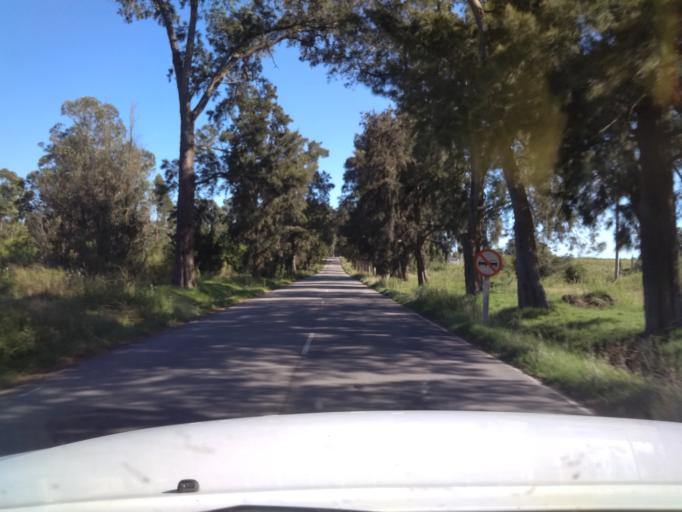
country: UY
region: Canelones
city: San Bautista
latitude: -34.3741
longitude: -55.9595
